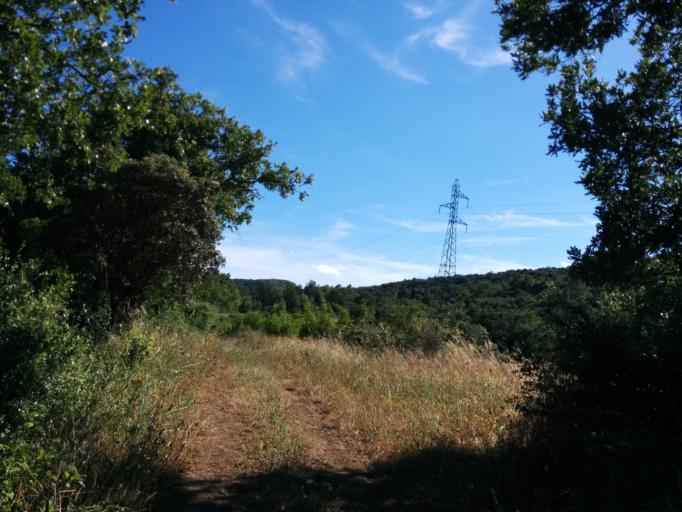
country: FR
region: Languedoc-Roussillon
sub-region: Departement du Gard
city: Saint-Christol-les-Ales
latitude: 44.0964
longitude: 4.0571
